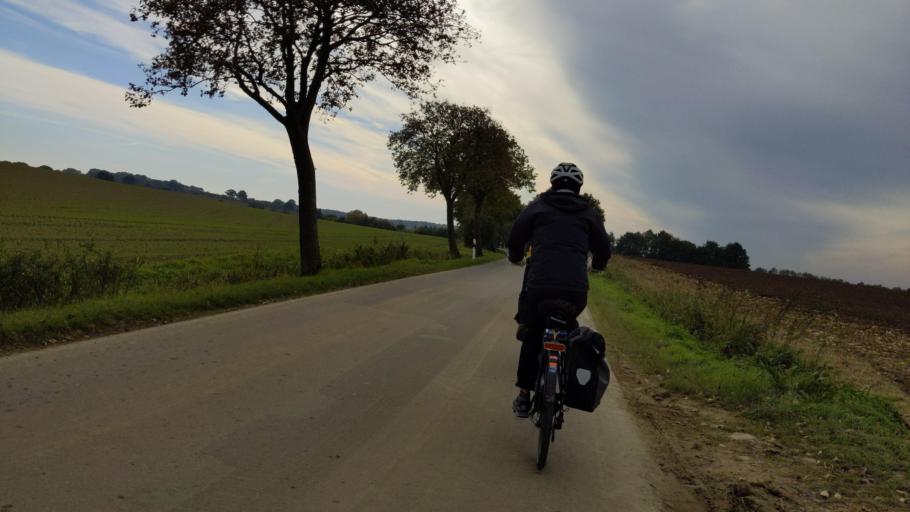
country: DE
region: Schleswig-Holstein
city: Rehhorst
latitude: 53.8877
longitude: 10.4762
